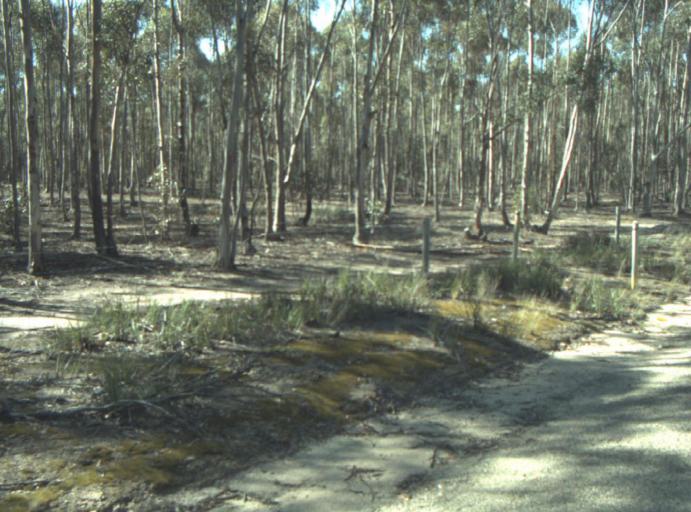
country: AU
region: Victoria
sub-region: Greater Geelong
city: Lara
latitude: -37.9440
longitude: 144.3920
